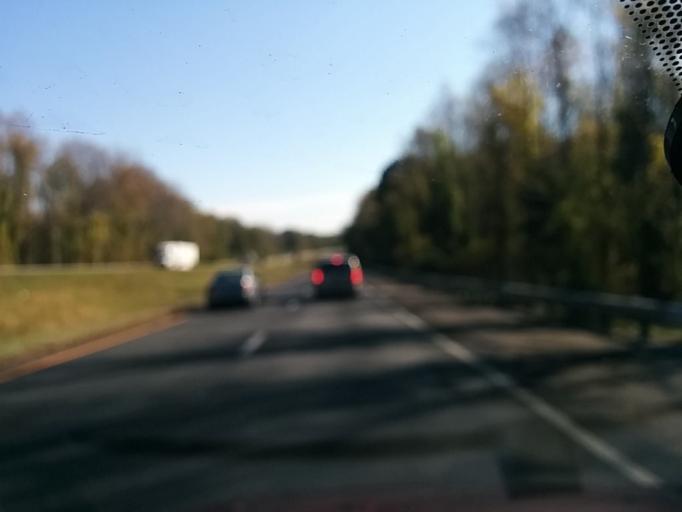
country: US
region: Virginia
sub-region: City of Charlottesville
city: Charlottesville
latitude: 38.0222
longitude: -78.5503
